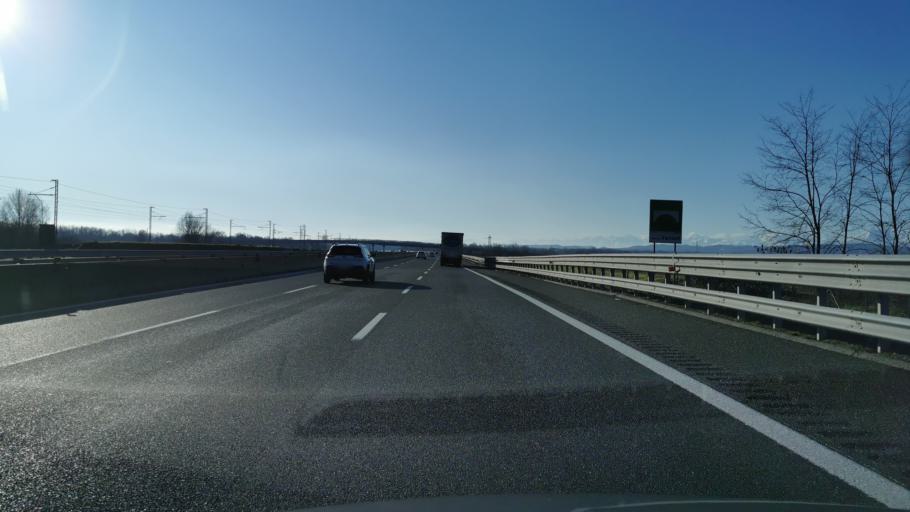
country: IT
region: Piedmont
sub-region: Provincia di Vercelli
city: Carisio
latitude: 45.4317
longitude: 8.2060
